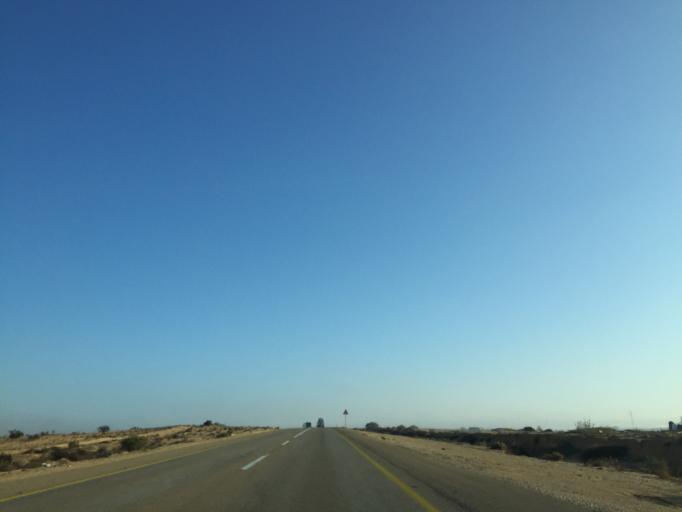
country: IL
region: Southern District
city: Yeroham
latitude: 31.0112
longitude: 34.9565
